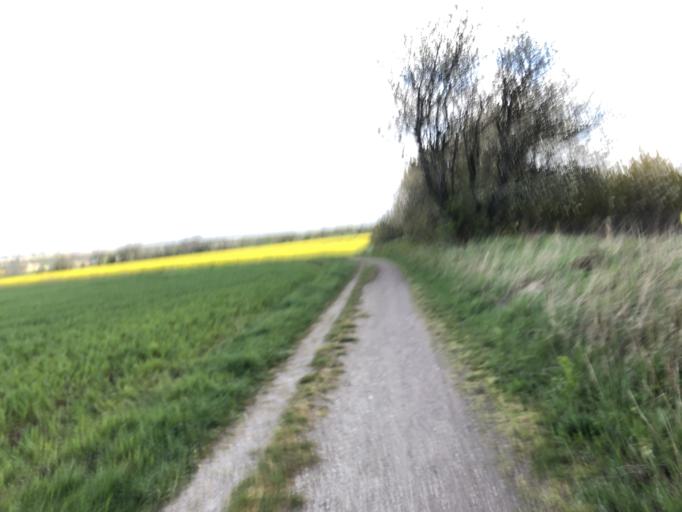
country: SE
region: Skane
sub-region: Lunds Kommun
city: Lund
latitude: 55.6971
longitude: 13.2871
